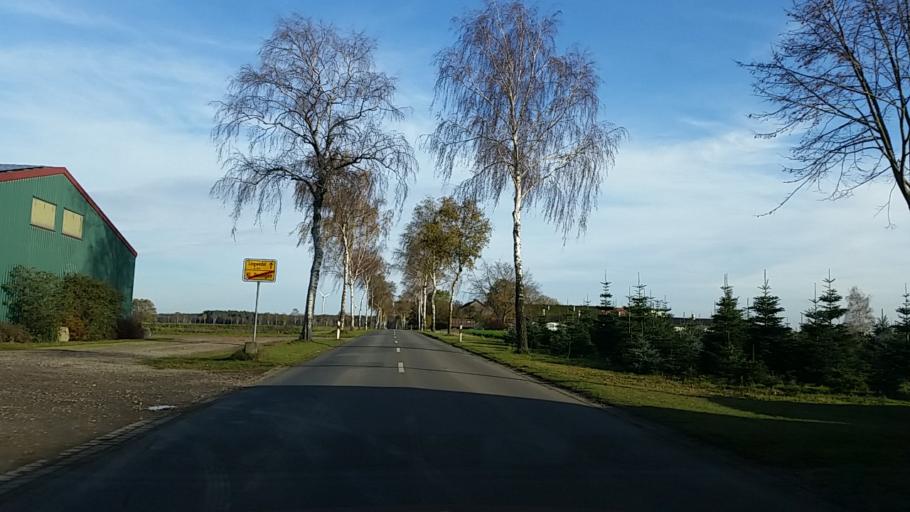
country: DE
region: Lower Saxony
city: Gross Oesingen
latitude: 52.6578
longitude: 10.4902
